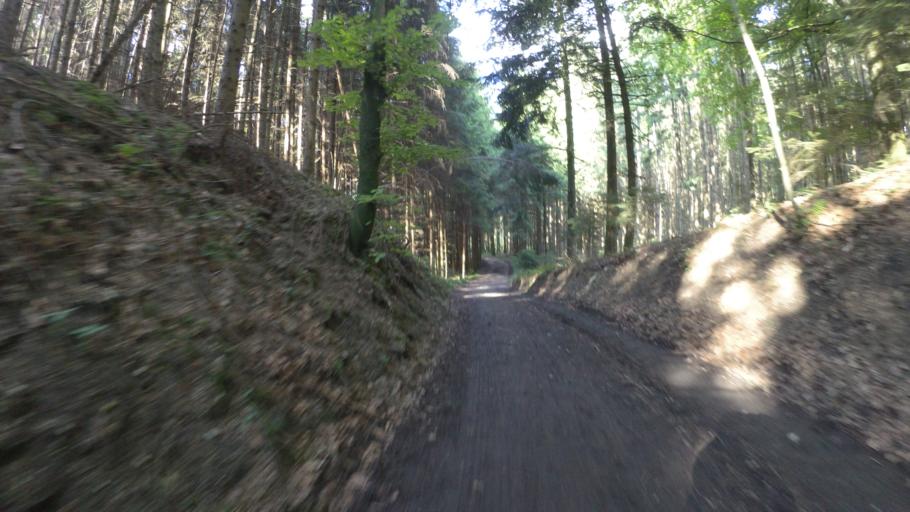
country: DE
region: Bavaria
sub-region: Upper Bavaria
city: Vachendorf
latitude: 47.8657
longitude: 12.6024
